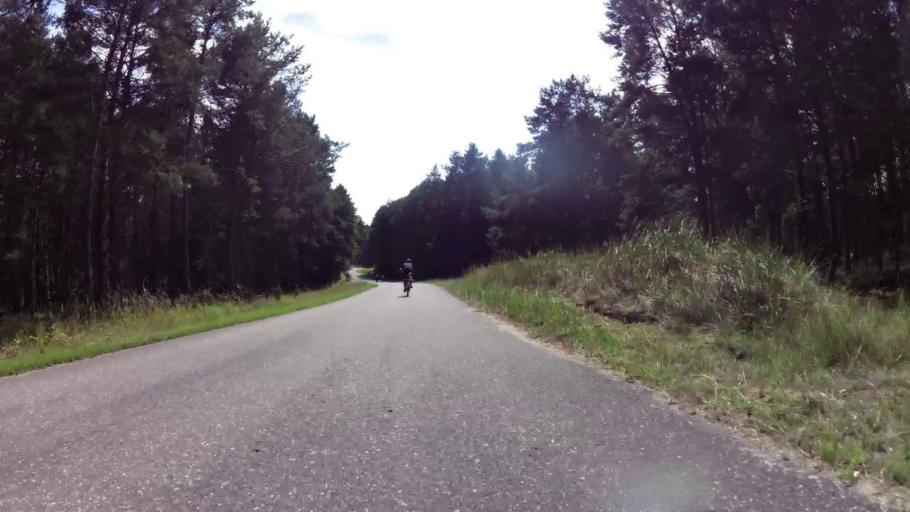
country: PL
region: West Pomeranian Voivodeship
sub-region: Powiat choszczenski
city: Drawno
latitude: 53.3588
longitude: 15.7052
